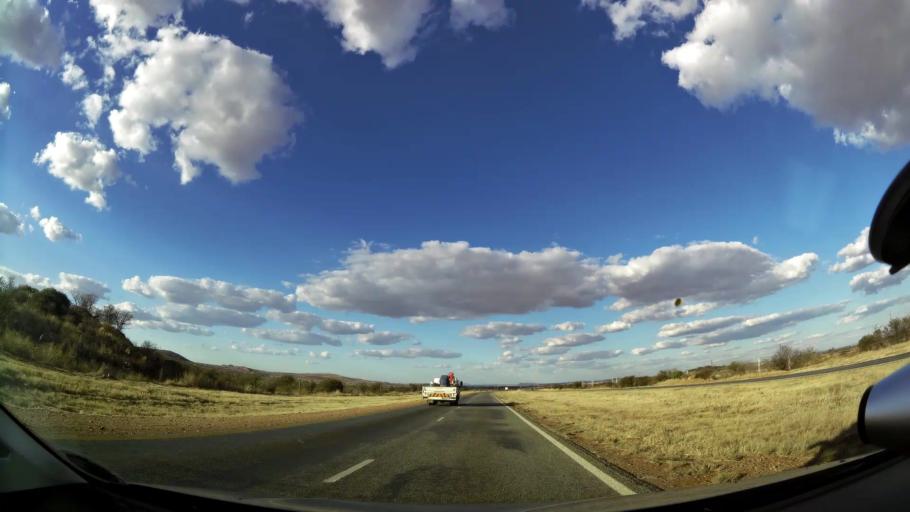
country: ZA
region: North-West
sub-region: Dr Kenneth Kaunda District Municipality
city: Potchefstroom
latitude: -26.7568
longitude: 26.9951
